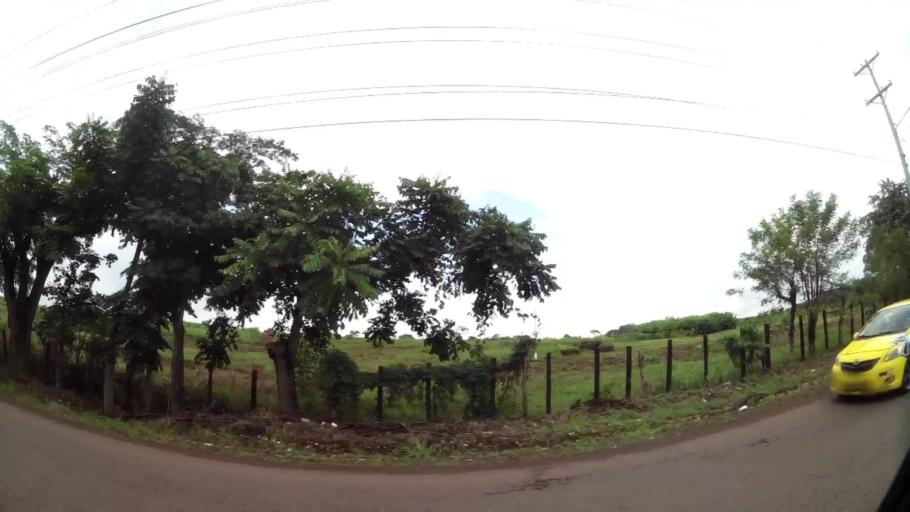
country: PA
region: Panama
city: Cabra Numero Uno
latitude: 9.1135
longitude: -79.3531
